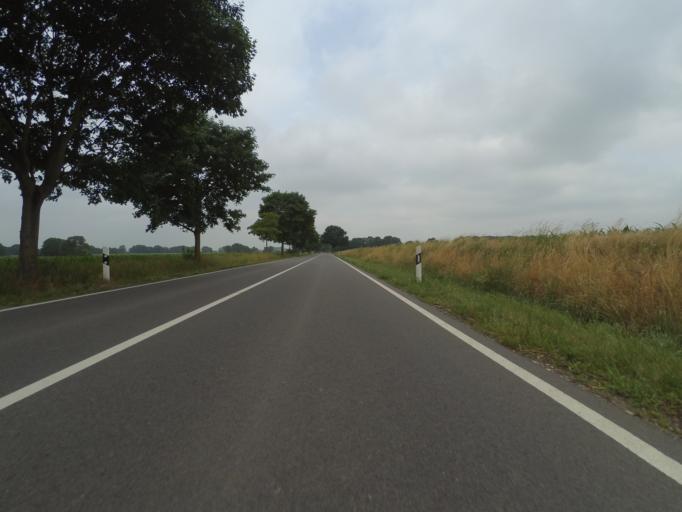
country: DE
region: Mecklenburg-Vorpommern
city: Domsuhl
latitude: 53.4822
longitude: 11.7554
